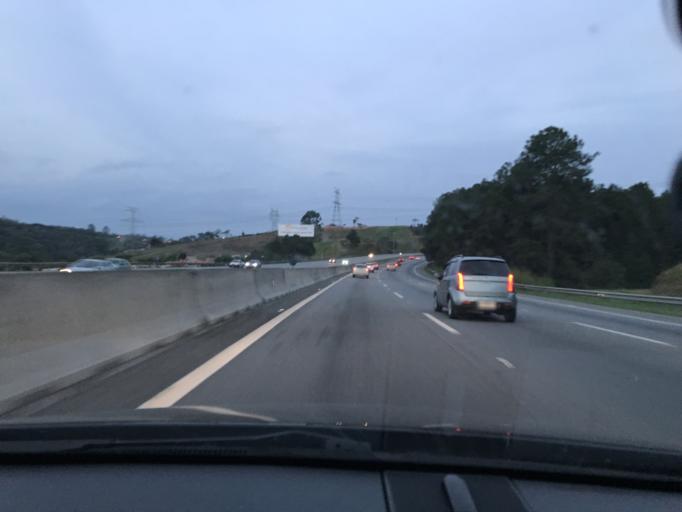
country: BR
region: Sao Paulo
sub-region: Aruja
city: Aruja
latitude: -23.4415
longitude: -46.2880
